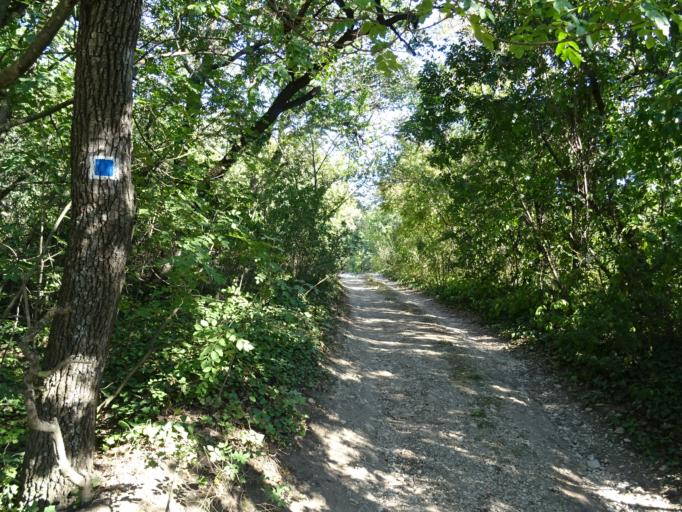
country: HU
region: Veszprem
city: Osi
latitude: 47.2068
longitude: 18.2030
